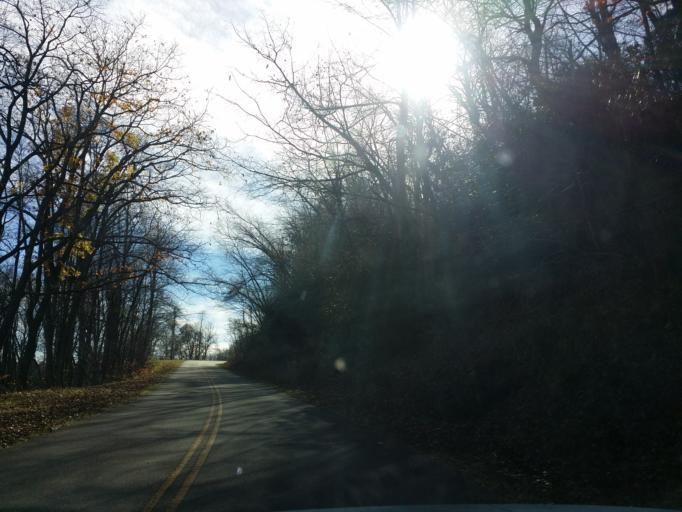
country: US
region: North Carolina
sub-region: McDowell County
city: Marion
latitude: 35.7669
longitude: -82.1673
